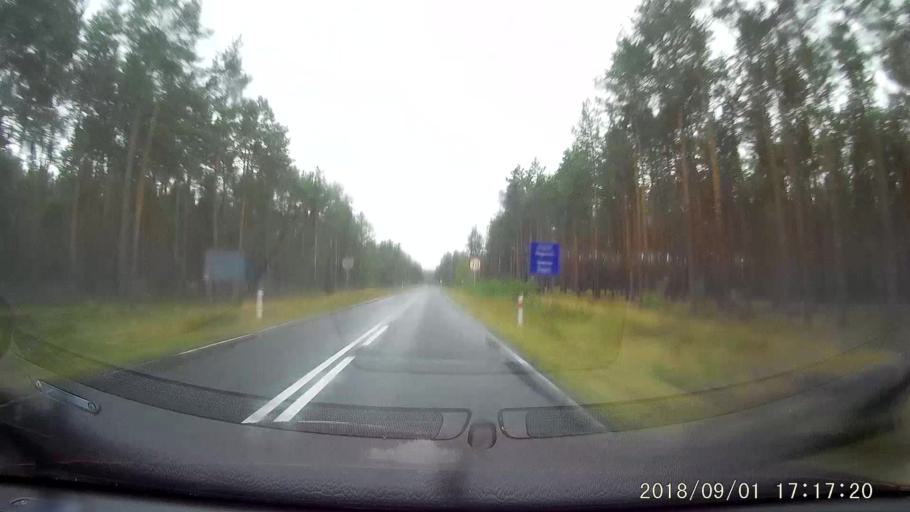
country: PL
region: Lubusz
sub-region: Powiat zielonogorski
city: Nowogrod Bobrzanski
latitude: 51.7518
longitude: 15.2712
